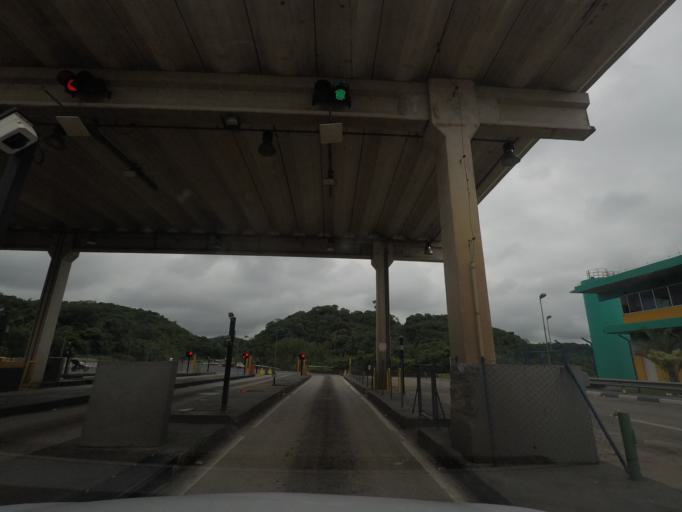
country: BR
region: Sao Paulo
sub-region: Juquia
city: Juquia
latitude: -24.3890
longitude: -47.7229
